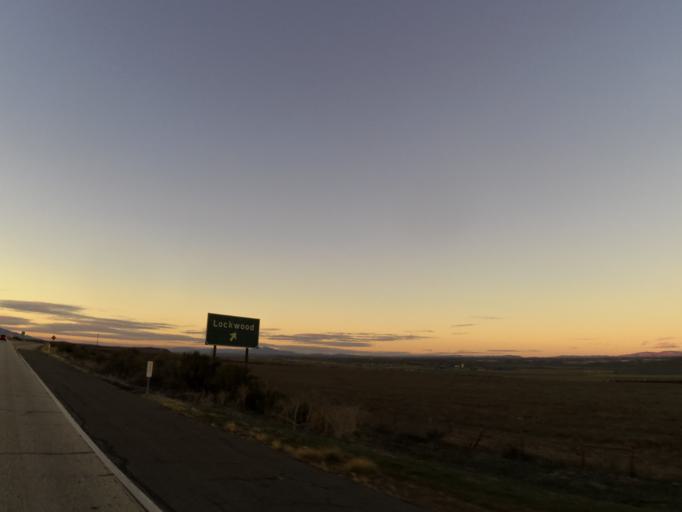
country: US
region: California
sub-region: Monterey County
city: King City
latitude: 36.0912
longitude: -121.0175
